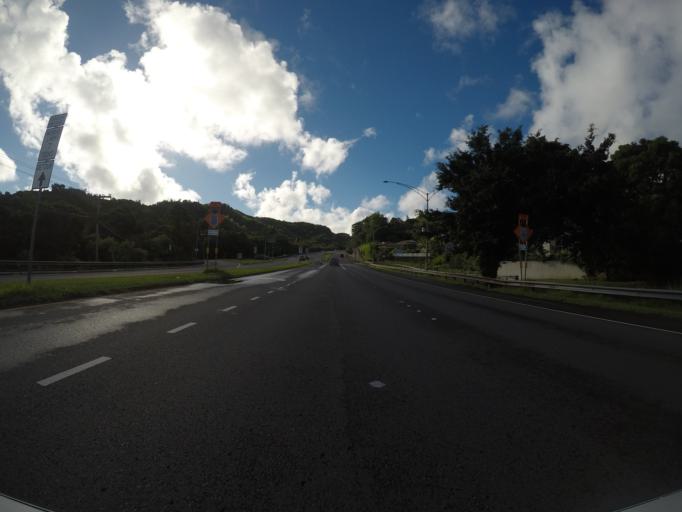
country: US
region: Hawaii
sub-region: Honolulu County
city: Kane'ohe
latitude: 21.4105
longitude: -157.7726
